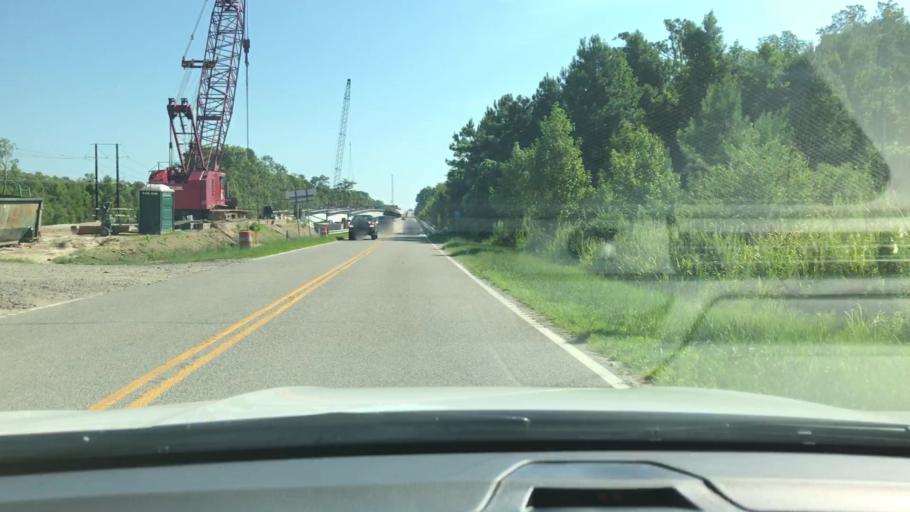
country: US
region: South Carolina
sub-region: Georgetown County
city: Murrells Inlet
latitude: 33.6537
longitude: -79.1640
